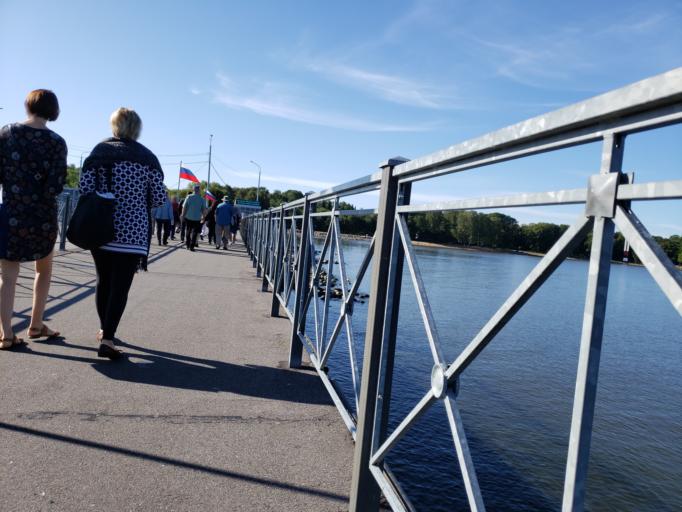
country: RU
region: St.-Petersburg
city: Peterhof
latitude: 59.8912
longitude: 29.9116
